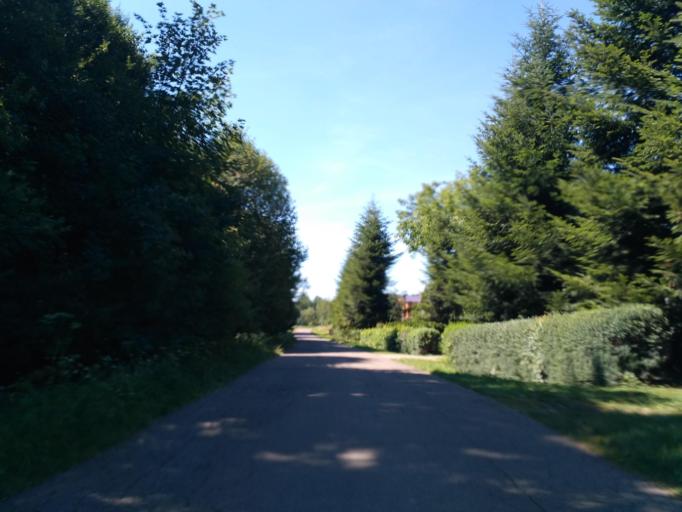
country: PL
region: Subcarpathian Voivodeship
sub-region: Powiat sanocki
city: Nowosielce-Gniewosz
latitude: 49.5352
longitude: 22.0493
